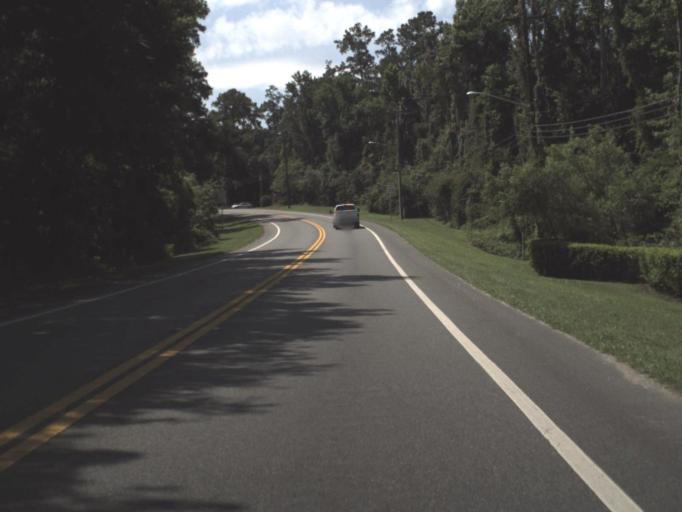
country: US
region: Florida
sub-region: Alachua County
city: Gainesville
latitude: 29.6326
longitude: -82.3260
